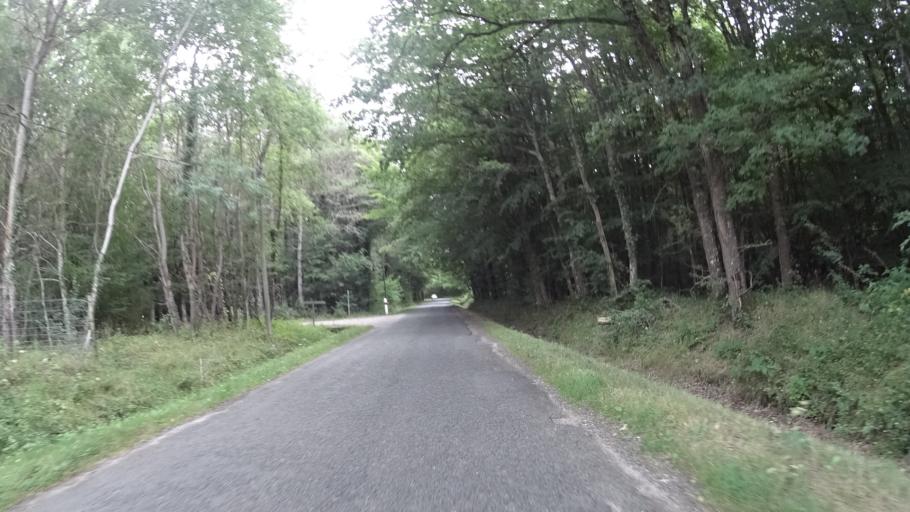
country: FR
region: Centre
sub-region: Departement du Loiret
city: Chevillon-sur-Huillard
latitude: 47.9477
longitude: 2.5970
